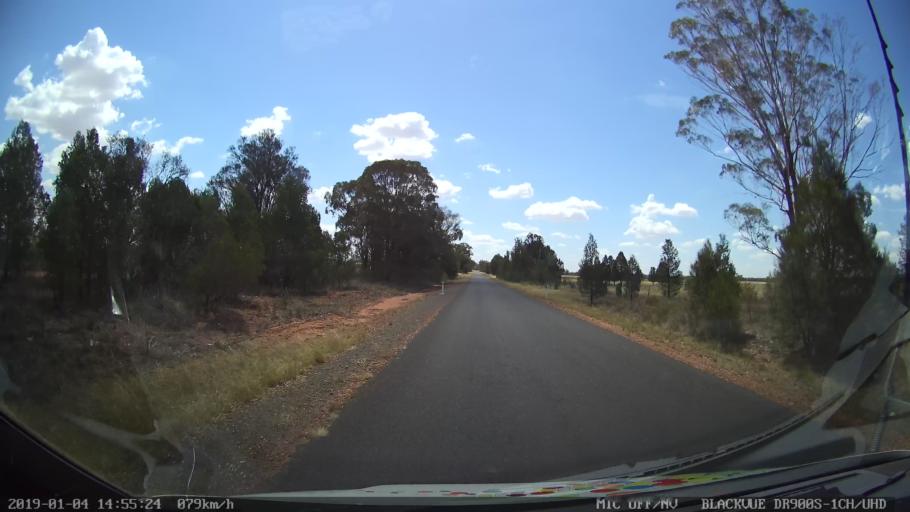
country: AU
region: New South Wales
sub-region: Dubbo Municipality
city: Dubbo
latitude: -31.9806
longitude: 148.6515
